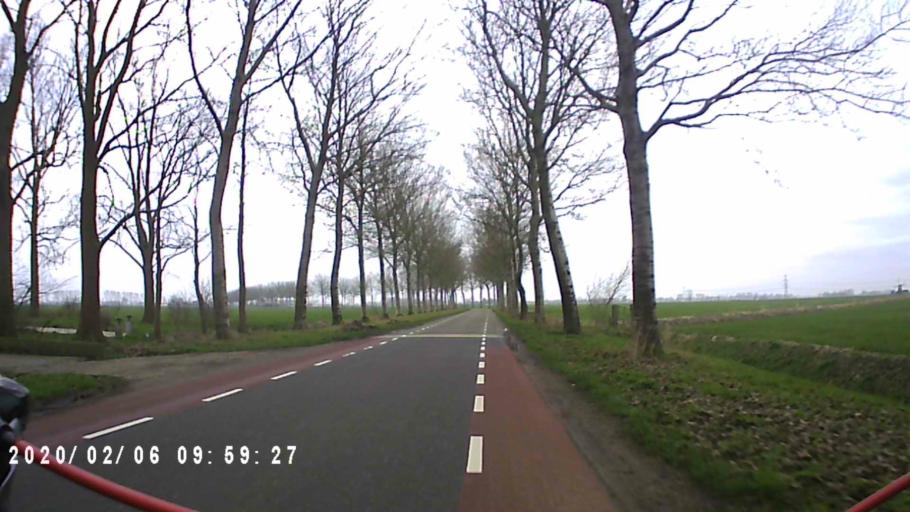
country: NL
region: Groningen
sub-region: Gemeente Zuidhorn
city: Aduard
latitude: 53.2685
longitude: 6.4936
